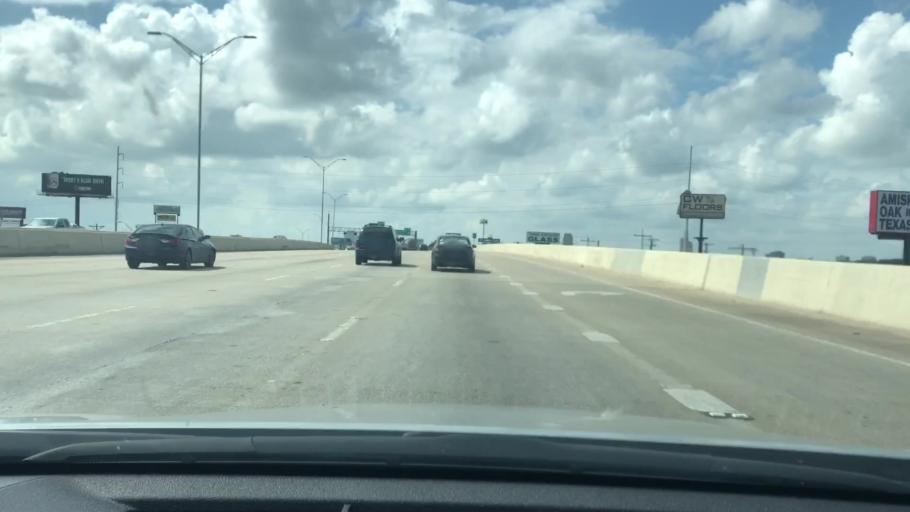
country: US
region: Texas
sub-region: Bexar County
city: Castle Hills
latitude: 29.5171
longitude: -98.5266
